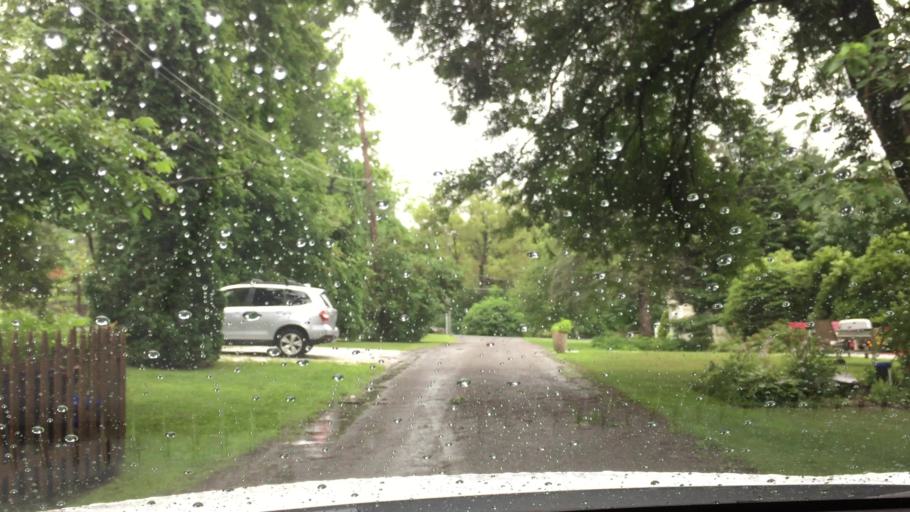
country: US
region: Massachusetts
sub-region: Berkshire County
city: Lenox
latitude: 42.4110
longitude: -73.3153
